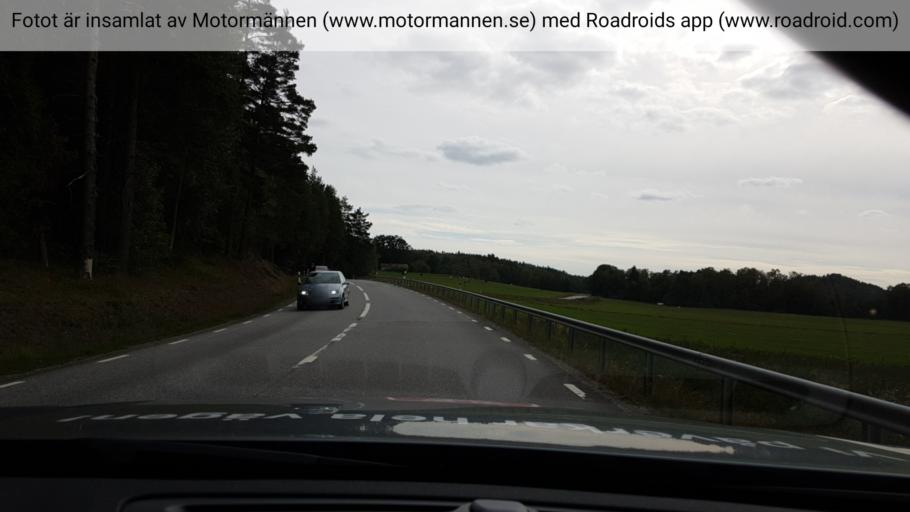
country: SE
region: Stockholm
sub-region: Botkyrka Kommun
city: Varsta
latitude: 59.1107
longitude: 17.8044
